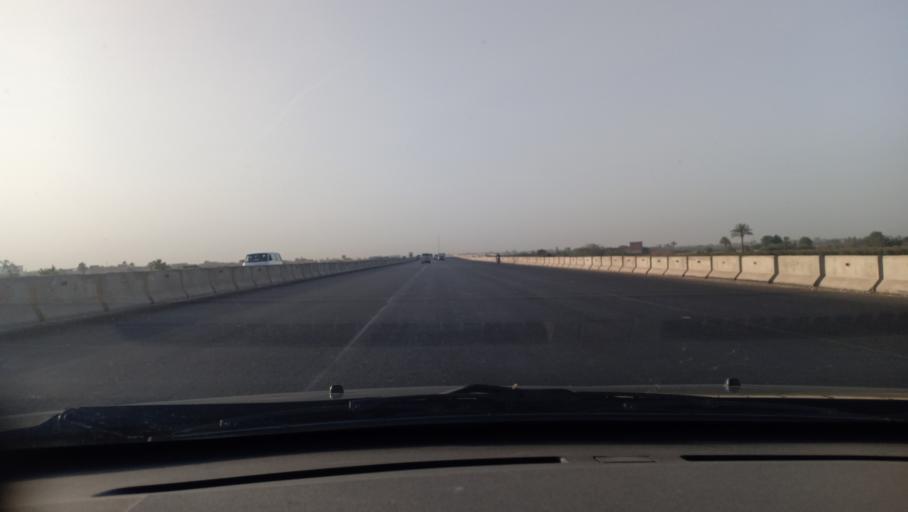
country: EG
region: Muhafazat al Qalyubiyah
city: Qalyub
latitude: 30.1855
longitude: 31.2417
